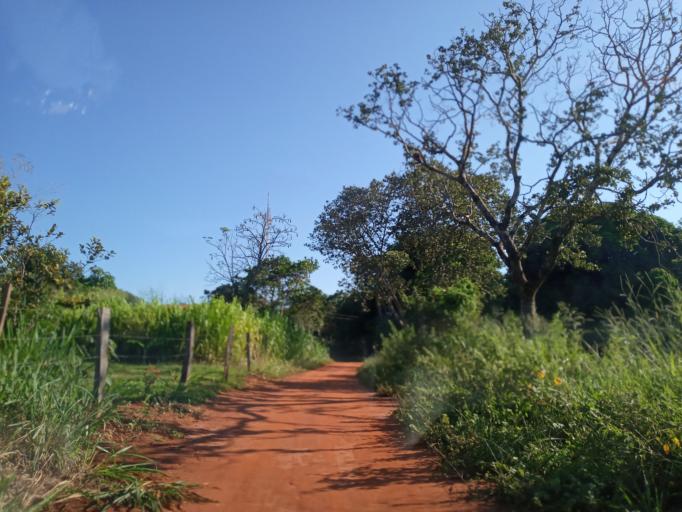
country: BR
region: Minas Gerais
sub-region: Ituiutaba
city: Ituiutaba
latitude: -18.9745
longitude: -49.4977
